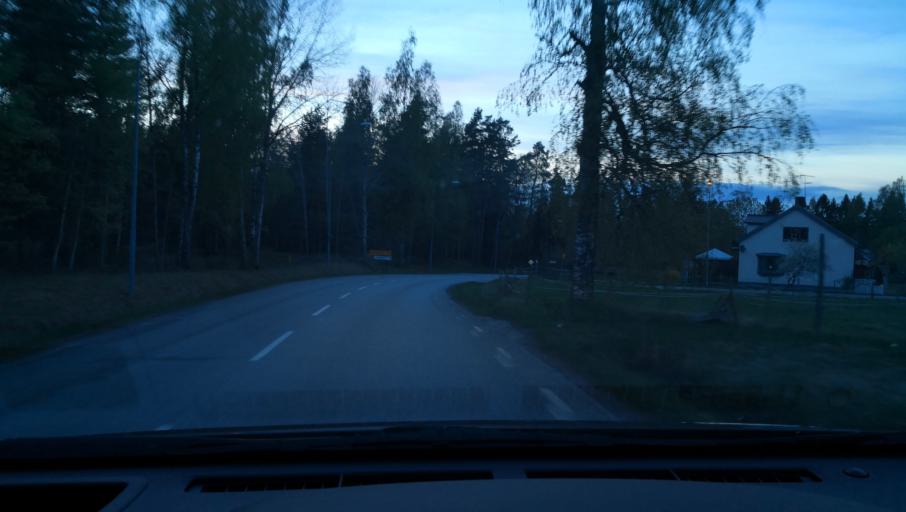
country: SE
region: OErebro
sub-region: Askersunds Kommun
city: Askersund
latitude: 59.0167
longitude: 14.8778
